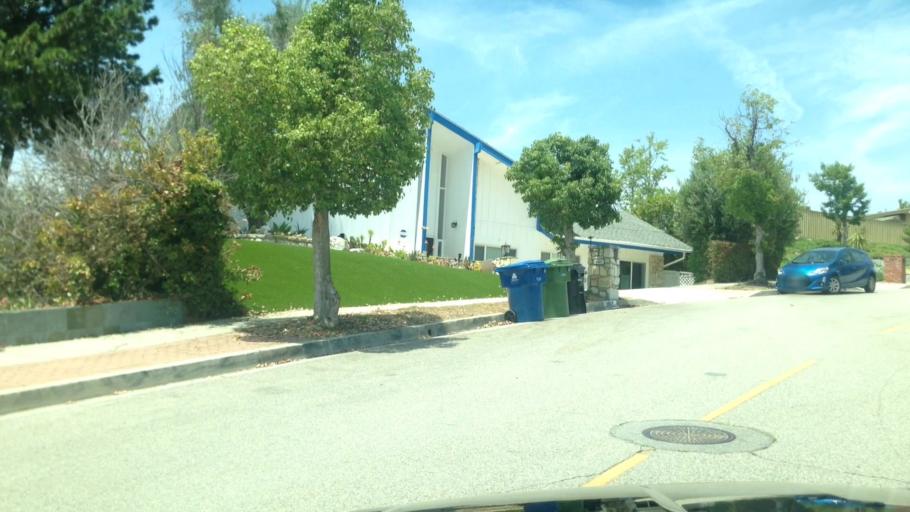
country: US
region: California
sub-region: Los Angeles County
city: Santa Monica
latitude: 34.0837
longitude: -118.5087
